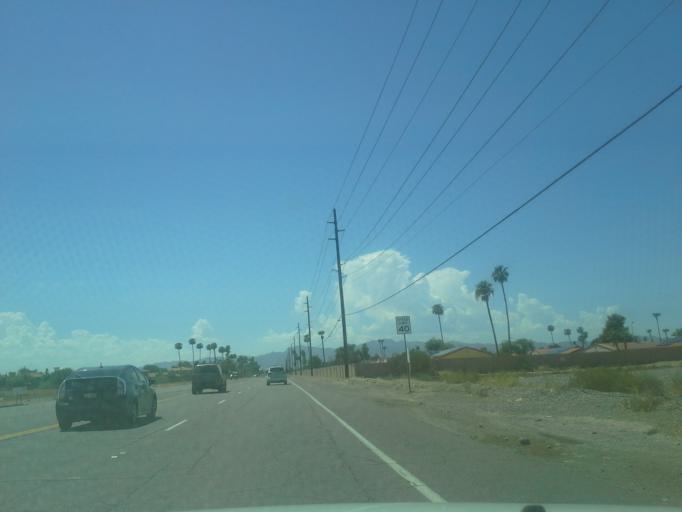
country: US
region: Arizona
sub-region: Maricopa County
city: Litchfield Park
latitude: 33.5369
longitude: -112.3416
